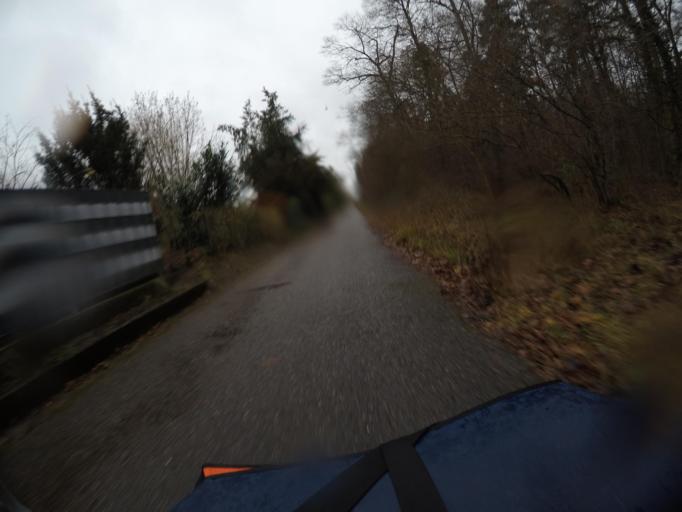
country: DE
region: Baden-Wuerttemberg
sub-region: Karlsruhe Region
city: Linkenheim-Hochstetten
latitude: 49.1013
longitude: 8.4702
